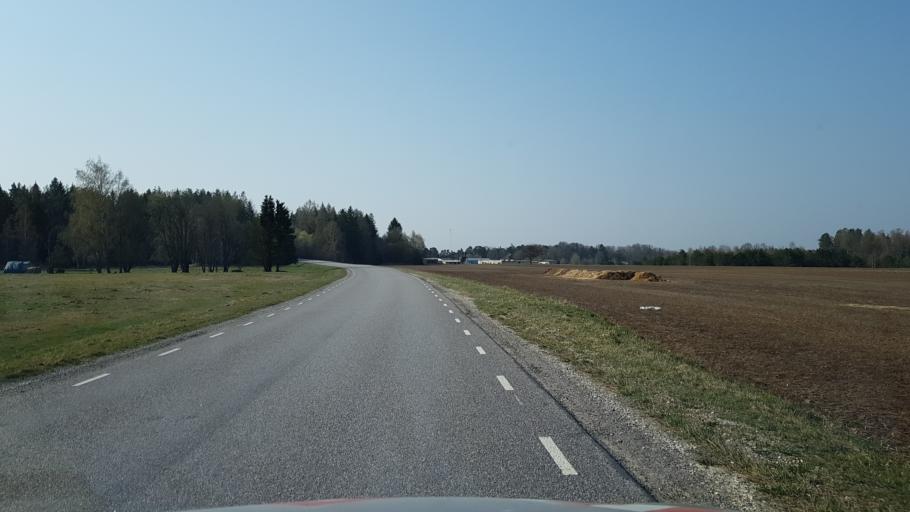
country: EE
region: Raplamaa
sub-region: Kohila vald
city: Kohila
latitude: 59.1814
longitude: 24.6568
